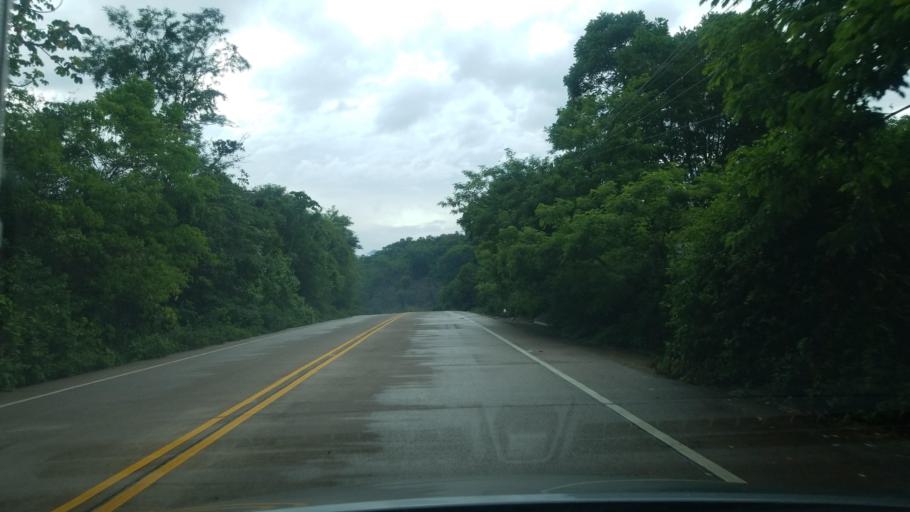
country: HN
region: Copan
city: Copan
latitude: 14.8563
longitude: -89.2075
